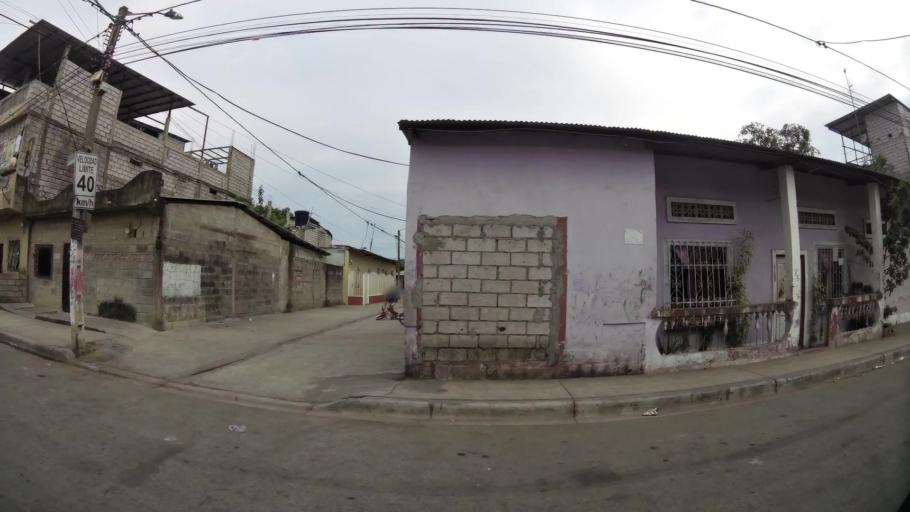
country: EC
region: Guayas
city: Guayaquil
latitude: -2.2623
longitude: -79.8799
